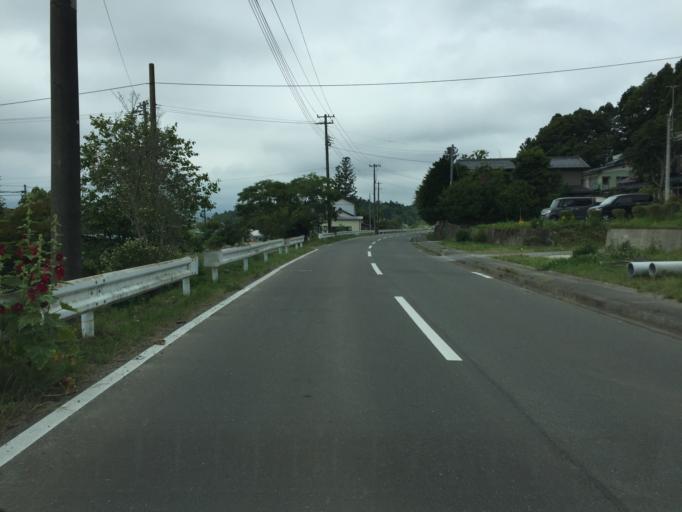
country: JP
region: Fukushima
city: Namie
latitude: 37.7120
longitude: 140.9801
